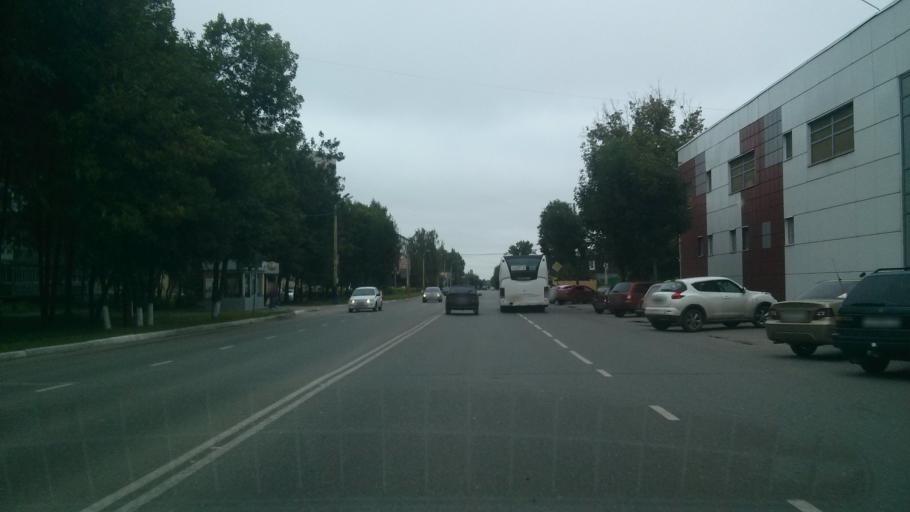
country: RU
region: Vladimir
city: Murom
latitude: 55.5710
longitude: 42.0584
